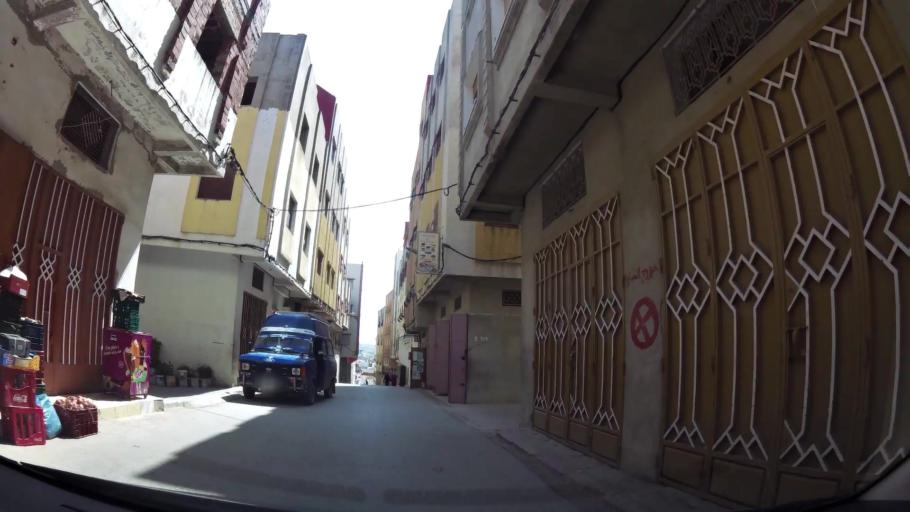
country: MA
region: Tanger-Tetouan
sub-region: Tanger-Assilah
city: Tangier
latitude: 35.7399
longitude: -5.8110
